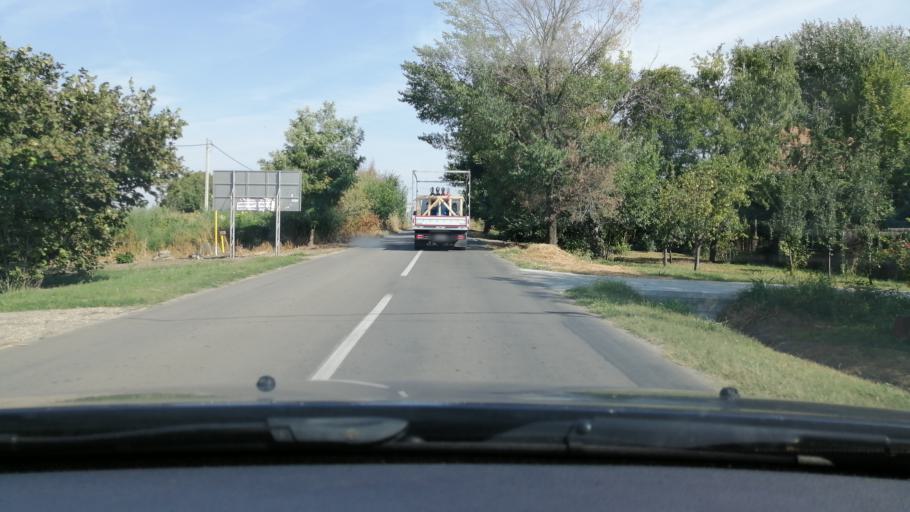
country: RS
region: Autonomna Pokrajina Vojvodina
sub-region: Juznobanatski Okrug
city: Kovacica
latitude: 45.1194
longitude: 20.6170
